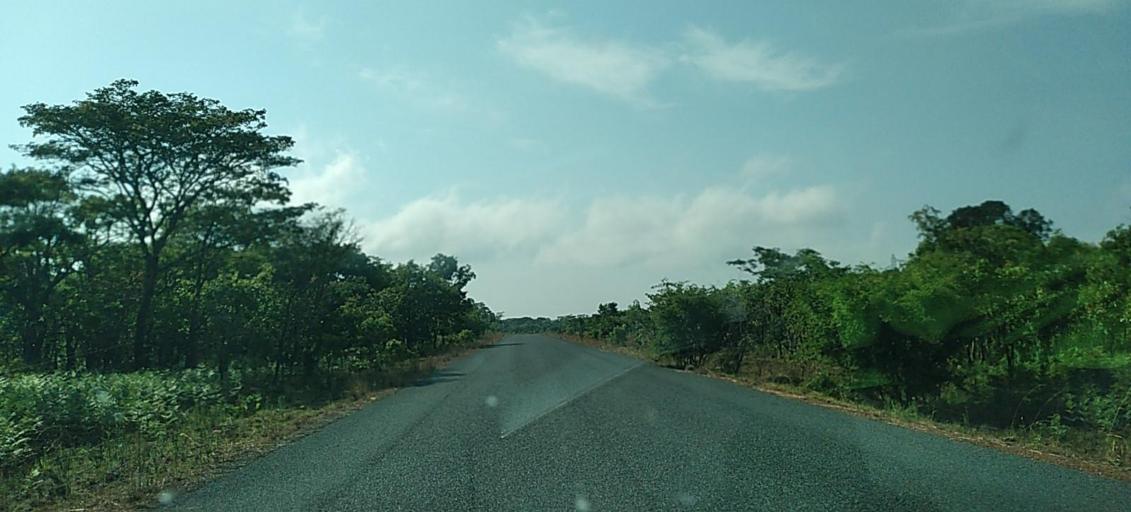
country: ZM
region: North-Western
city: Mwinilunga
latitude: -11.7427
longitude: 24.9871
